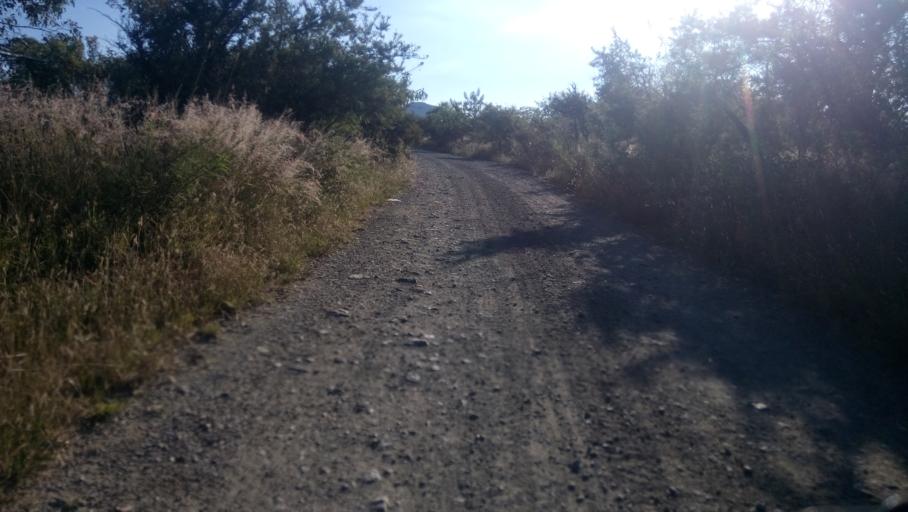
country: MX
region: Guanajuato
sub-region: Leon
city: Medina
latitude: 21.1950
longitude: -101.6204
